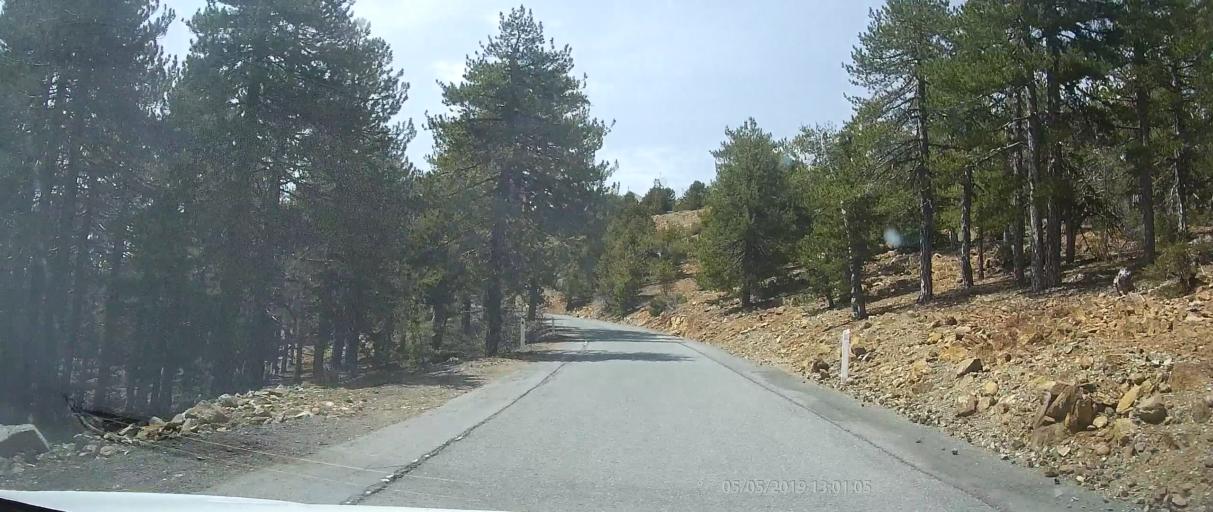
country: CY
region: Lefkosia
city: Kakopetria
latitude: 34.9349
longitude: 32.8662
